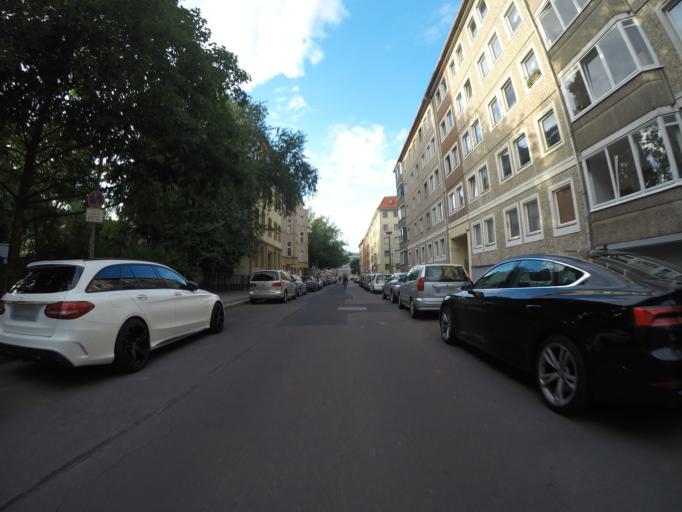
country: DE
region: Berlin
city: Berlin
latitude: 52.5250
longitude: 13.4094
